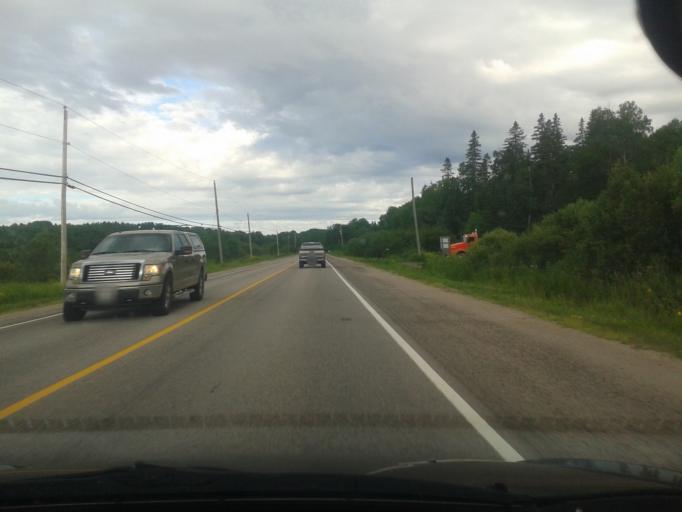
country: CA
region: Ontario
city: Powassan
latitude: 46.1896
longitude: -79.3066
